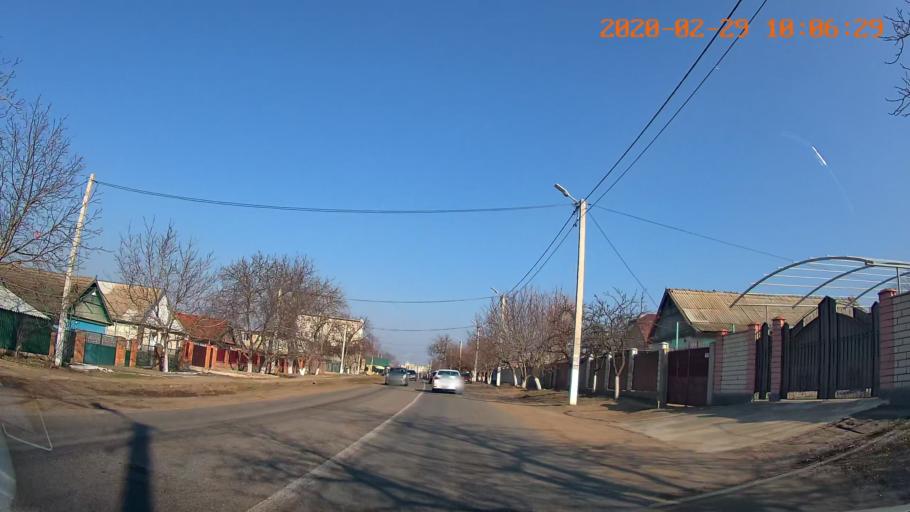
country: MD
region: Telenesti
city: Tiraspolul Nou
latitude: 46.8150
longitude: 29.6691
